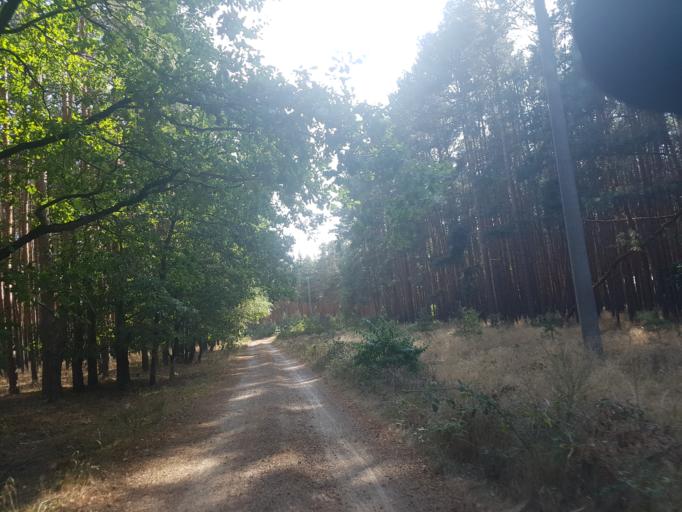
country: DE
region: Saxony-Anhalt
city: Jessen
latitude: 51.8642
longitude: 13.0337
